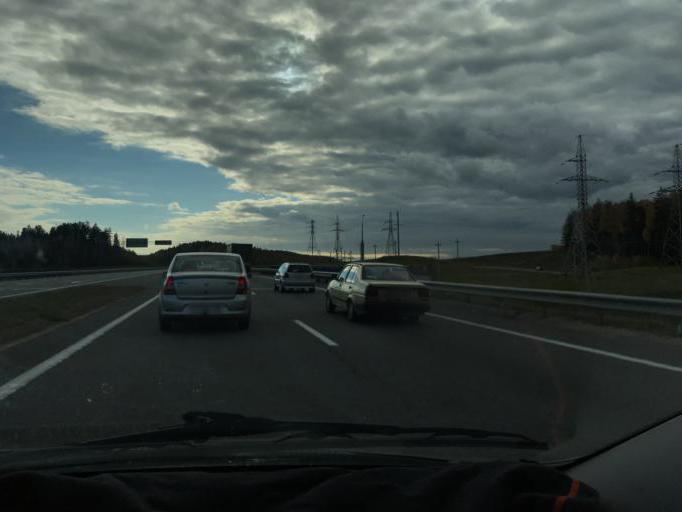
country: BY
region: Minsk
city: Lahoysk
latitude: 54.2081
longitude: 27.8225
